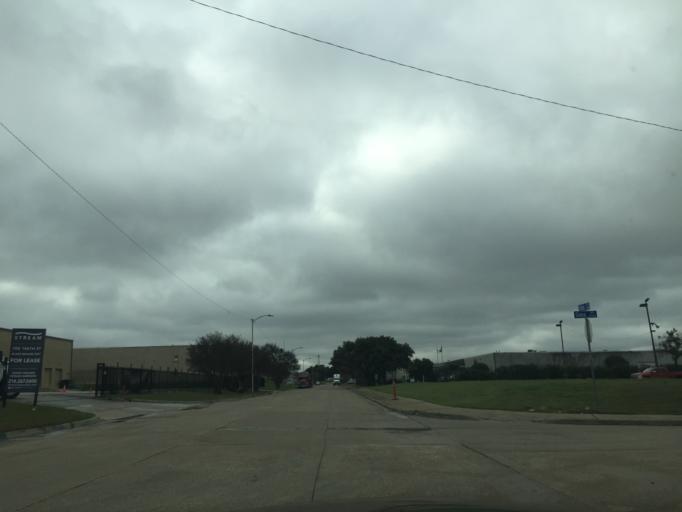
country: US
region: Texas
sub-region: Tarrant County
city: Arlington
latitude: 32.7538
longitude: -97.0600
